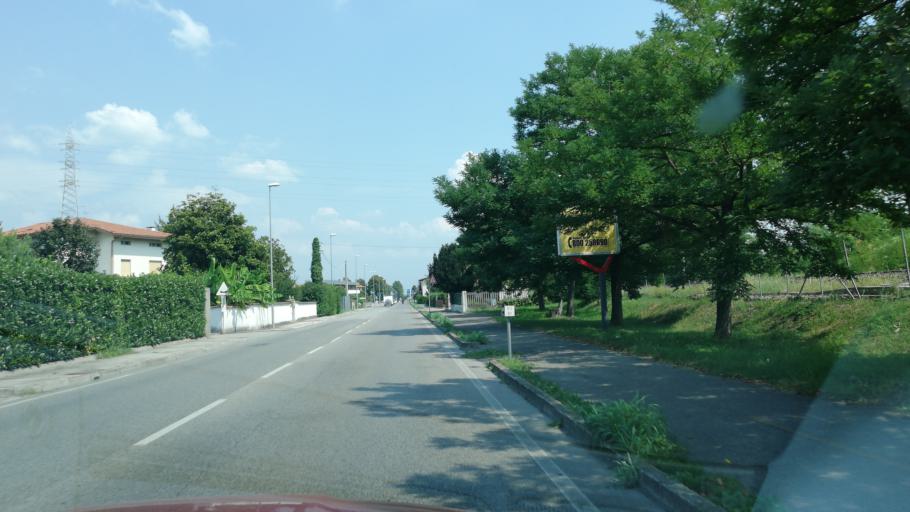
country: IT
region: Friuli Venezia Giulia
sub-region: Provincia di Udine
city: Latisana
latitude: 45.7862
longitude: 13.0091
